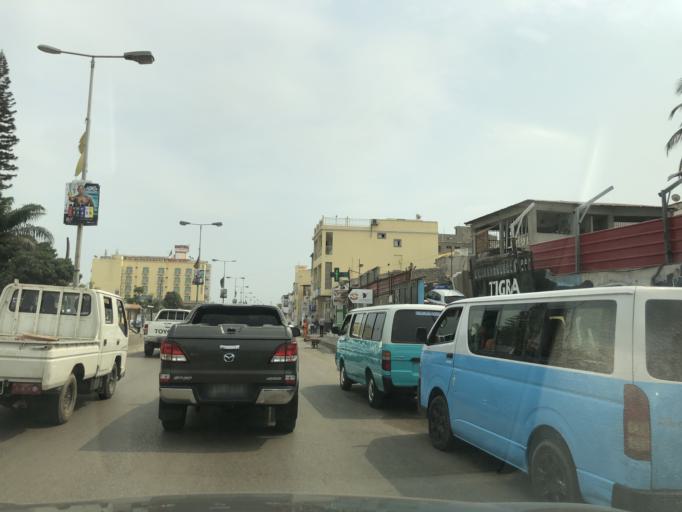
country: AO
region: Luanda
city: Luanda
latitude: -8.8444
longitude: 13.2126
